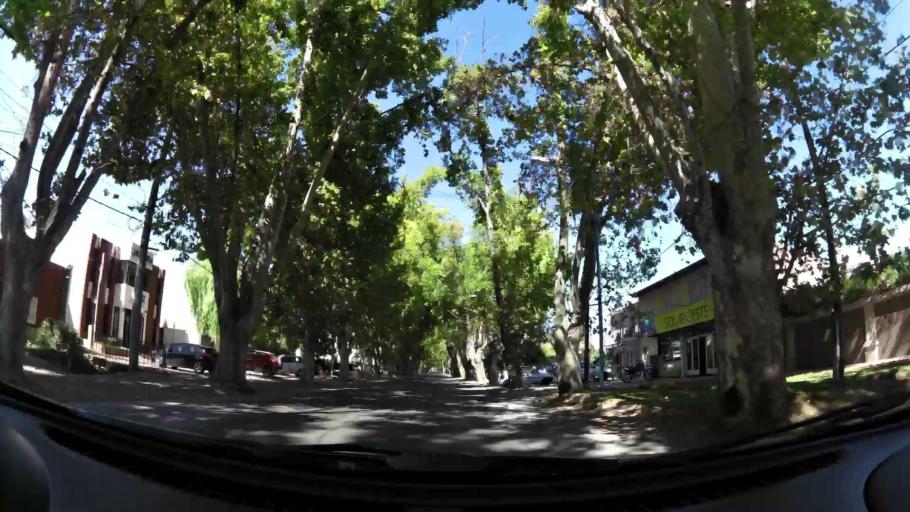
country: AR
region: Mendoza
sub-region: Departamento de Godoy Cruz
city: Godoy Cruz
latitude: -32.9490
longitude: -68.8441
